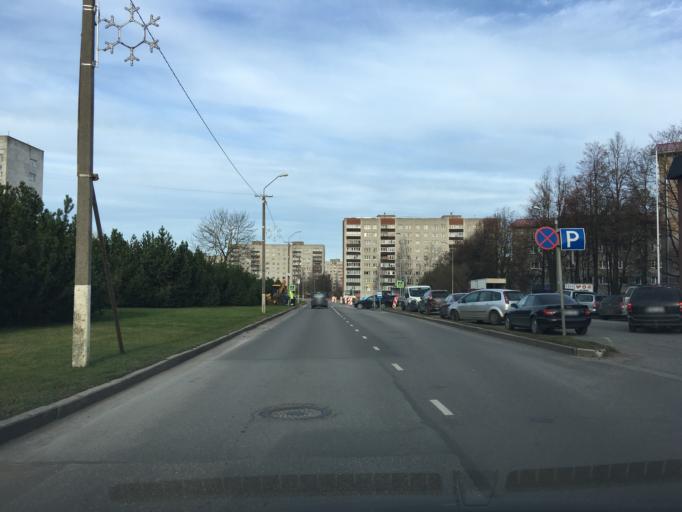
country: EE
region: Ida-Virumaa
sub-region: Narva linn
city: Narva
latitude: 59.3812
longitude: 28.1801
